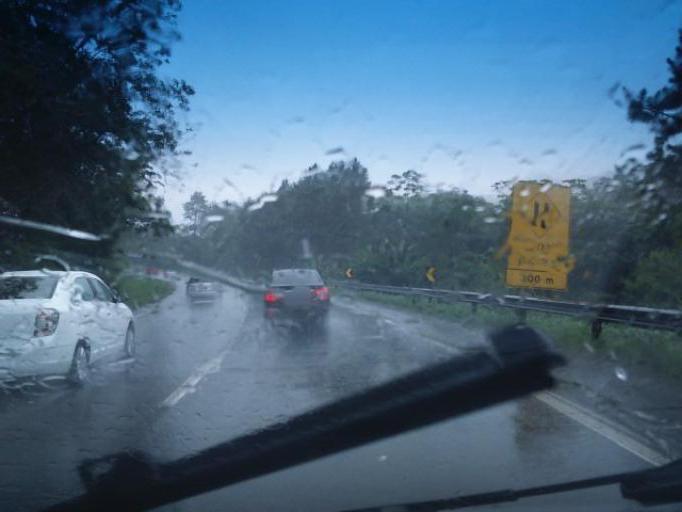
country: BR
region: Parana
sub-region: Guaratuba
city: Guaratuba
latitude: -25.9131
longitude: -48.9192
